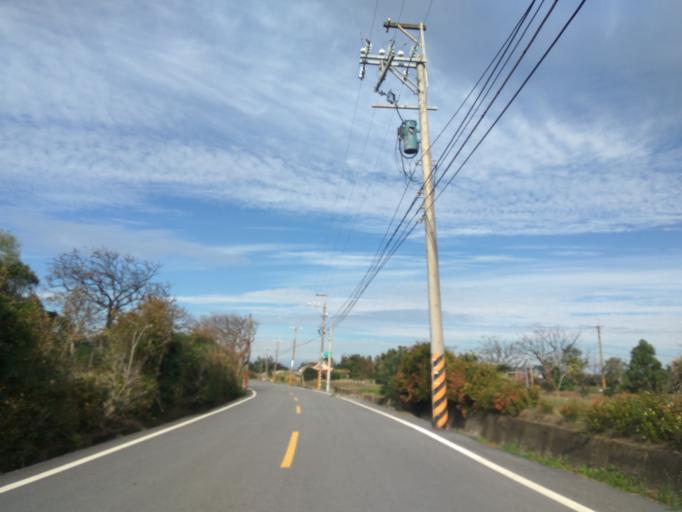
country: TW
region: Taiwan
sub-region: Hsinchu
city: Zhubei
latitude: 25.0018
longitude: 121.0865
